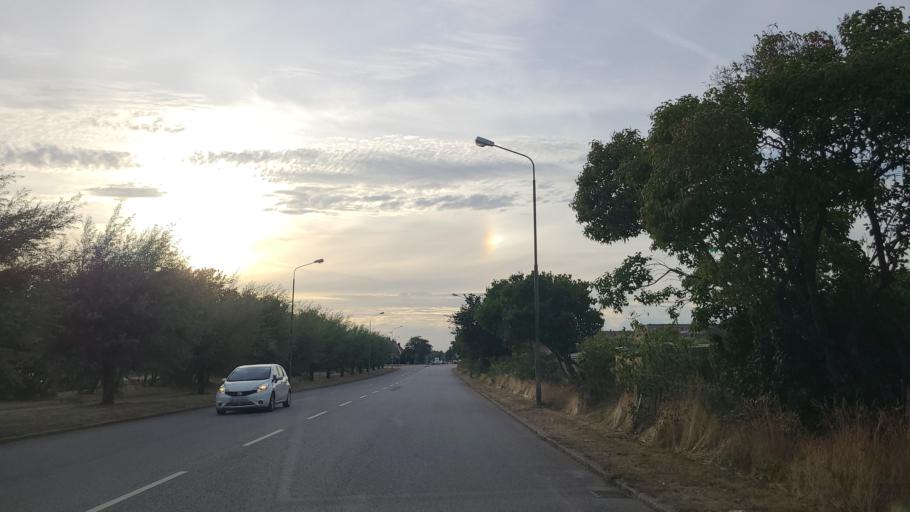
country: SE
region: Skane
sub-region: Malmo
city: Malmoe
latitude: 55.5770
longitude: 12.9823
